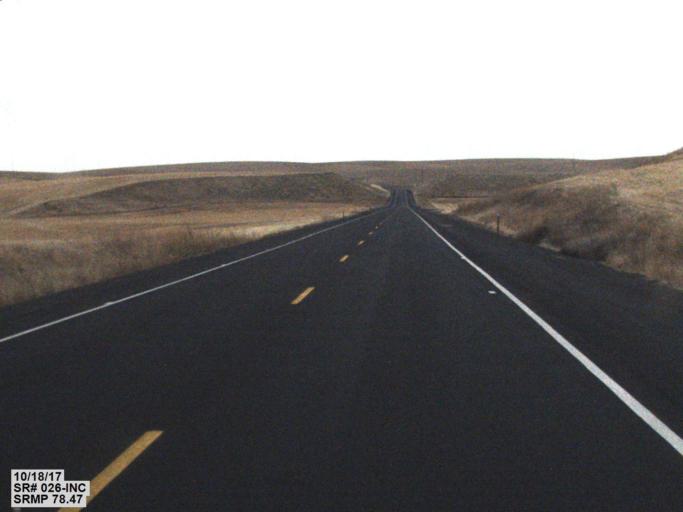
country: US
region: Washington
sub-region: Adams County
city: Ritzville
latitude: 46.7884
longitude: -118.3863
